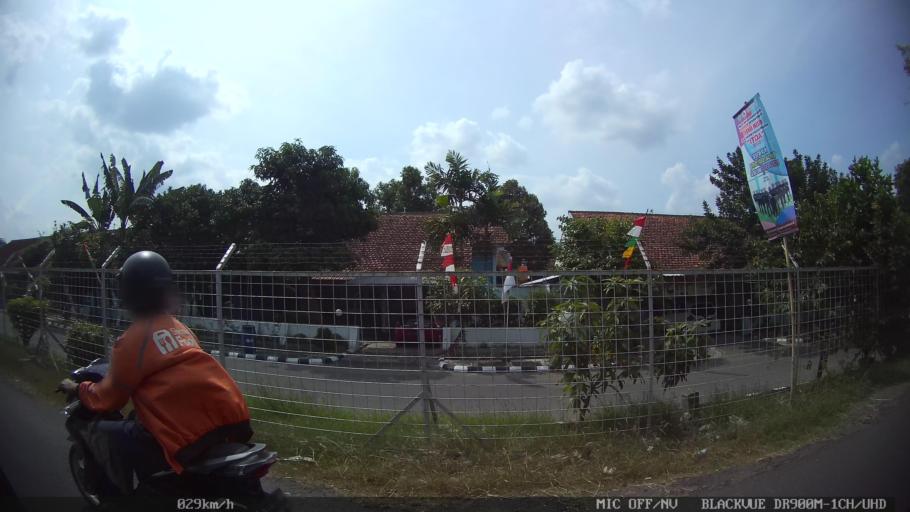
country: ID
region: Daerah Istimewa Yogyakarta
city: Depok
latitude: -7.7986
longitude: 110.4153
